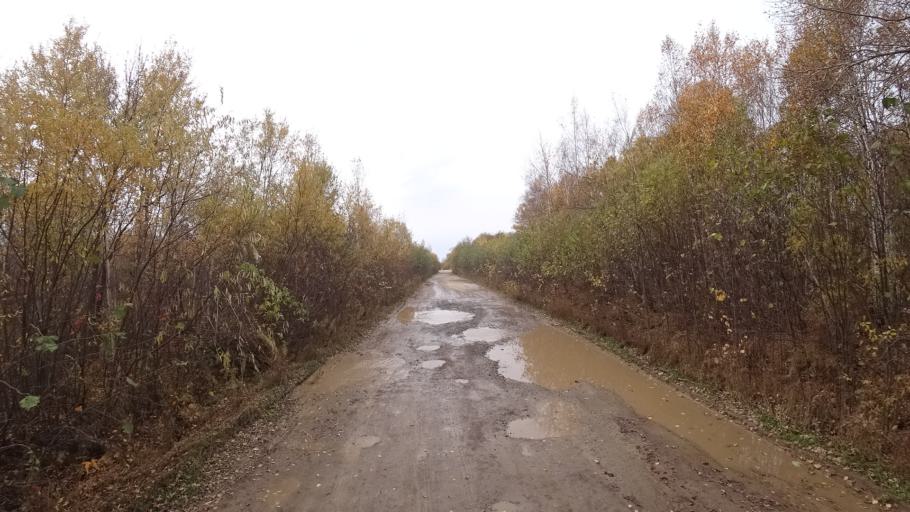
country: RU
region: Khabarovsk Krai
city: Amursk
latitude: 50.1438
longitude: 136.9657
